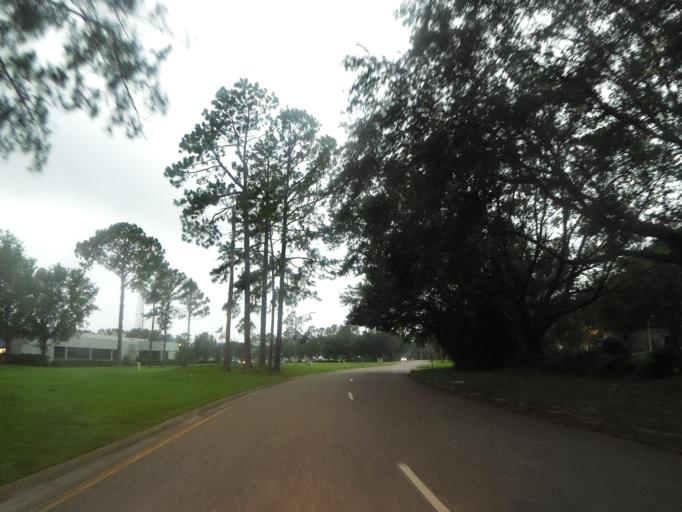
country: US
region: Florida
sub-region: Duval County
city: Neptune Beach
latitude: 30.2824
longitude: -81.5120
